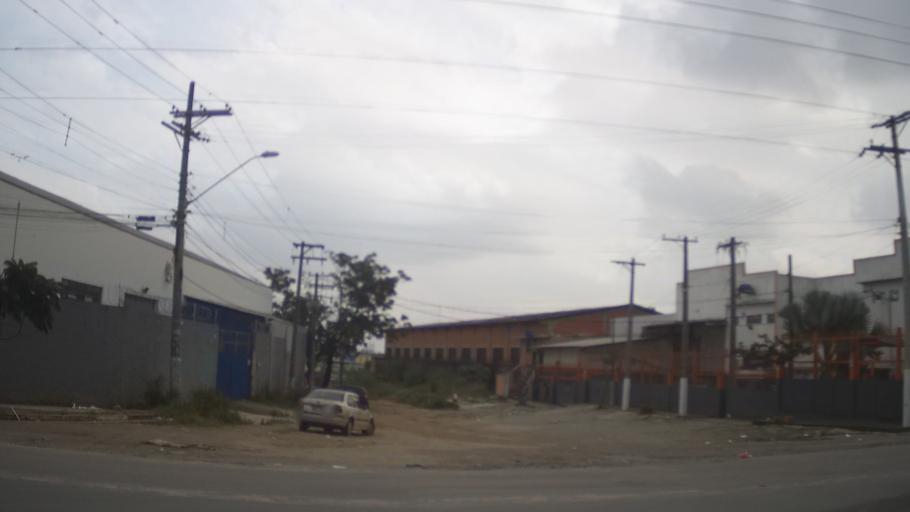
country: BR
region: Sao Paulo
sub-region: Guarulhos
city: Guarulhos
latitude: -23.4649
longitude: -46.4702
